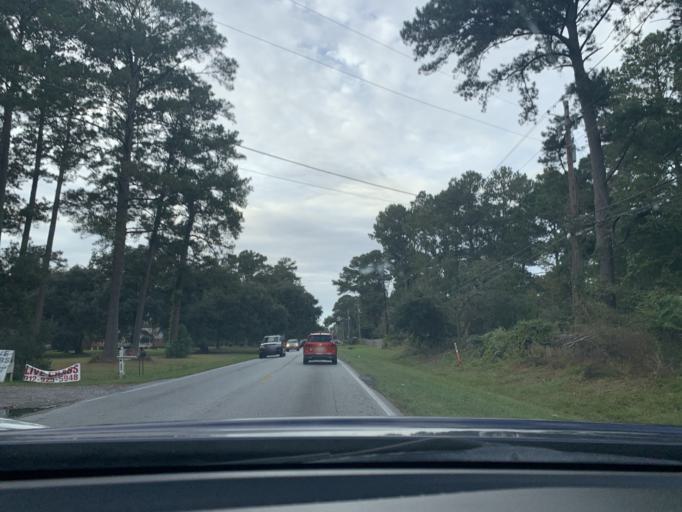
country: US
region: Georgia
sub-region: Chatham County
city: Georgetown
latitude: 32.0210
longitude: -81.2404
